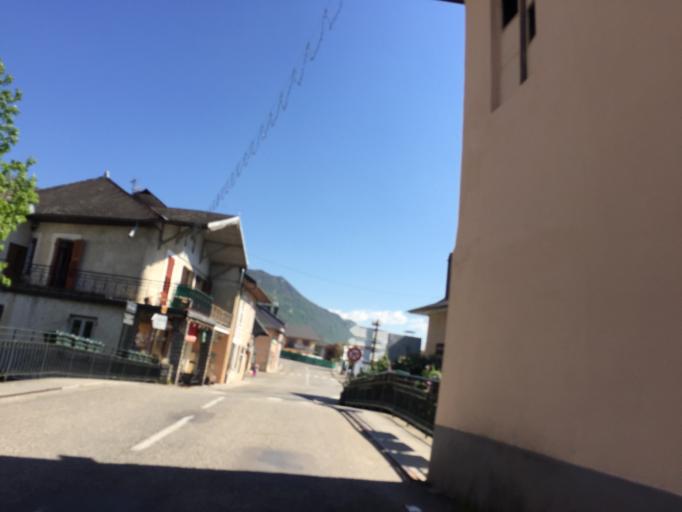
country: FR
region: Rhone-Alpes
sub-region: Departement de la Savoie
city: Barby
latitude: 45.5776
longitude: 5.9738
